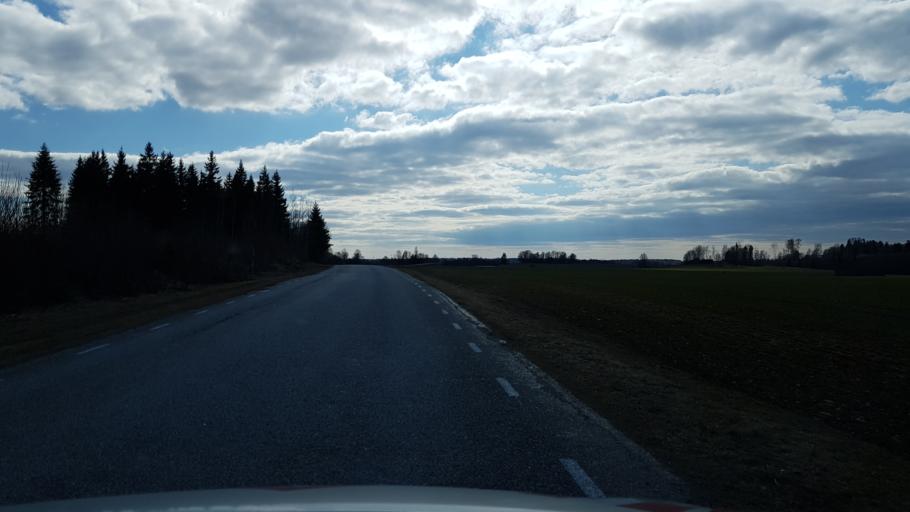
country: EE
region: Laeaene-Virumaa
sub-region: Kadrina vald
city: Kadrina
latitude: 59.3007
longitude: 26.2184
